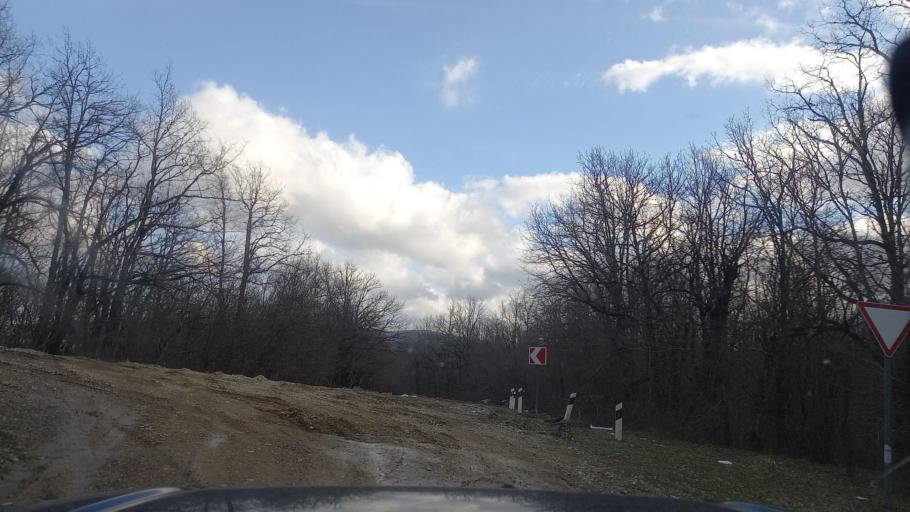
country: RU
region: Krasnodarskiy
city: Smolenskaya
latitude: 44.5754
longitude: 38.8057
